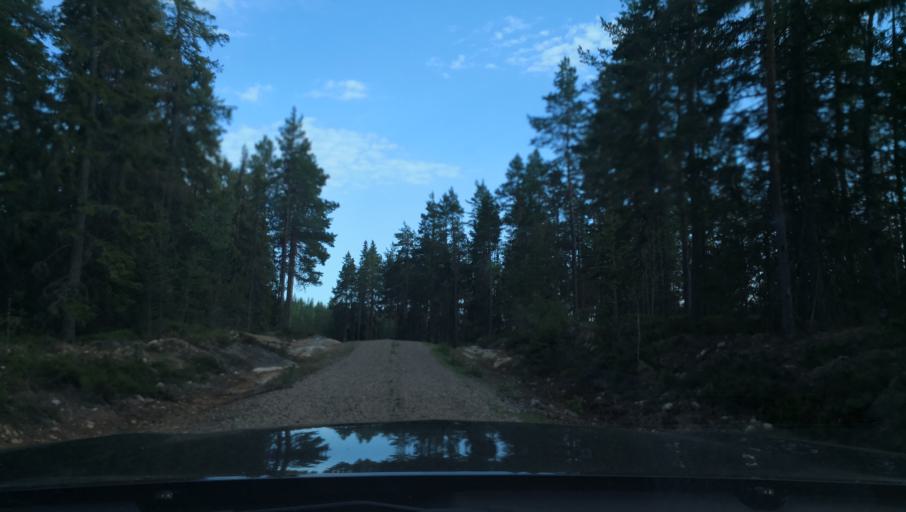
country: SE
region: Dalarna
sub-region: Smedjebackens Kommun
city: Smedjebacken
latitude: 60.0676
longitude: 15.3076
